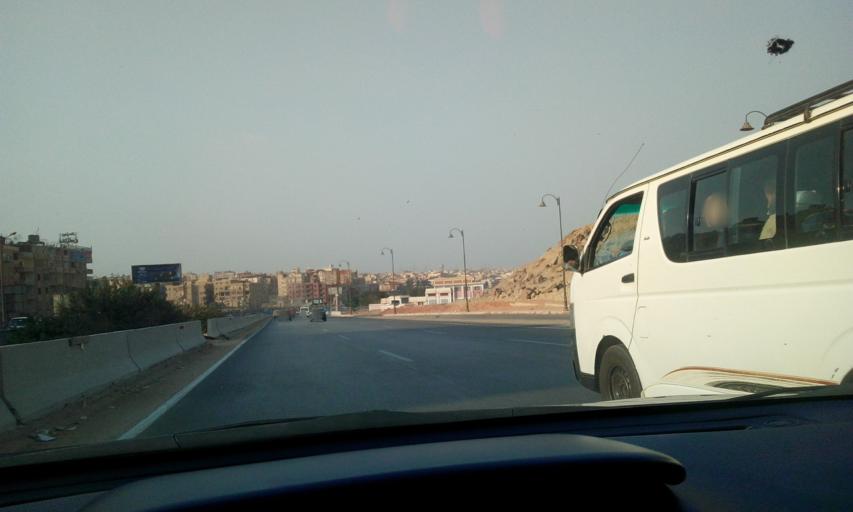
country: EG
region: Al Jizah
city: Al Jizah
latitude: 29.9673
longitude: 31.1086
